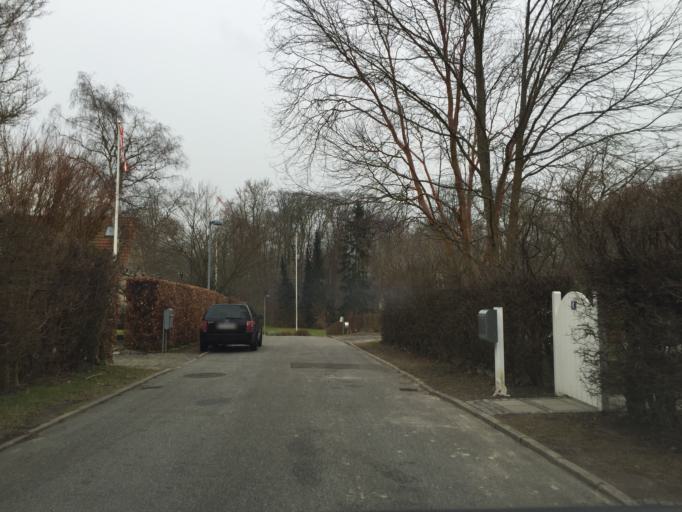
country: DK
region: Capital Region
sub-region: Fureso Kommune
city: Farum
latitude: 55.8083
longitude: 12.3635
